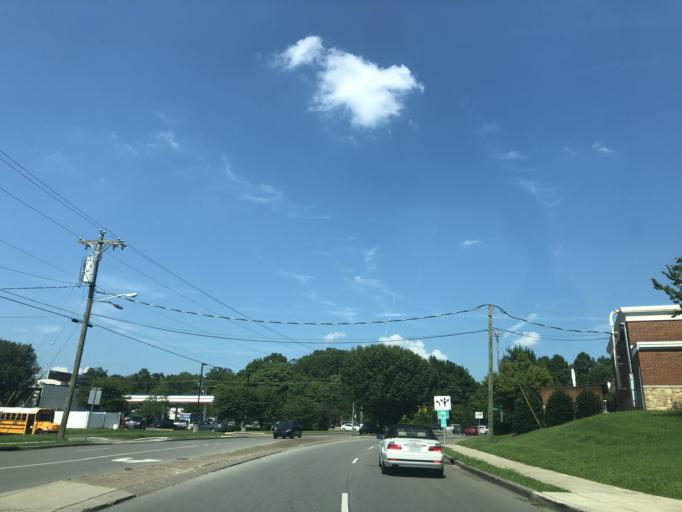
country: US
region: Tennessee
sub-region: Davidson County
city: Lakewood
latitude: 36.1520
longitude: -86.6266
